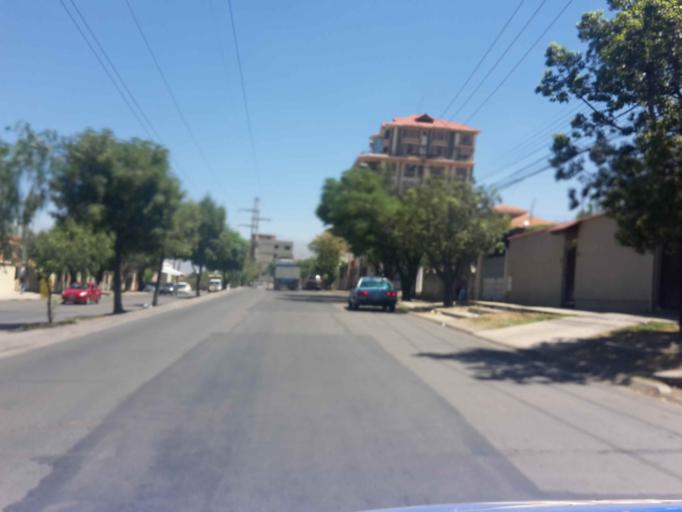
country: BO
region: Cochabamba
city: Cochabamba
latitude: -17.3699
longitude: -66.1425
